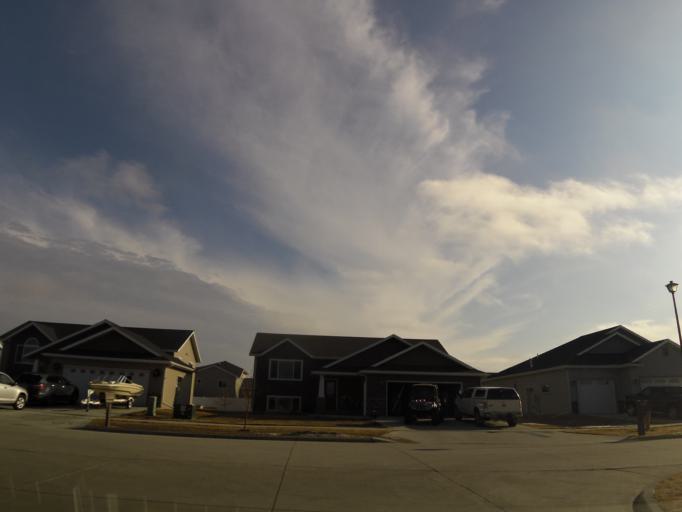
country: US
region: North Dakota
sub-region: Grand Forks County
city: Grand Forks
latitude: 47.8806
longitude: -97.0632
